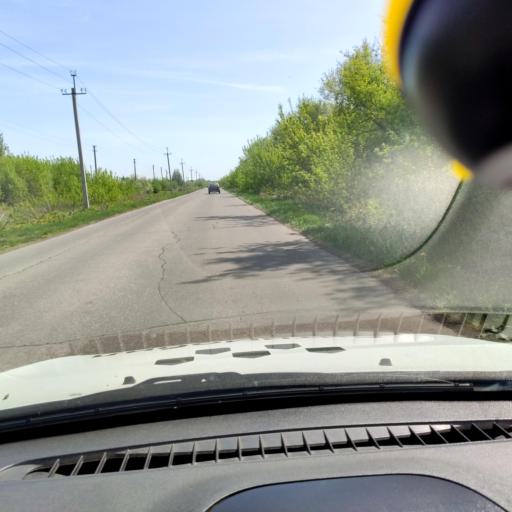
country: RU
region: Samara
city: Tol'yatti
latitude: 53.6646
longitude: 49.3452
